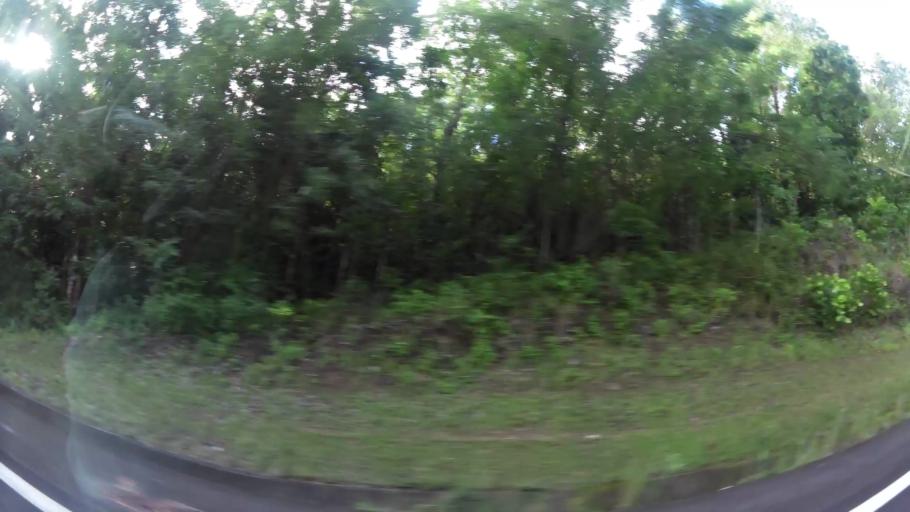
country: MQ
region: Martinique
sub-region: Martinique
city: Ducos
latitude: 14.5990
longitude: -60.9462
